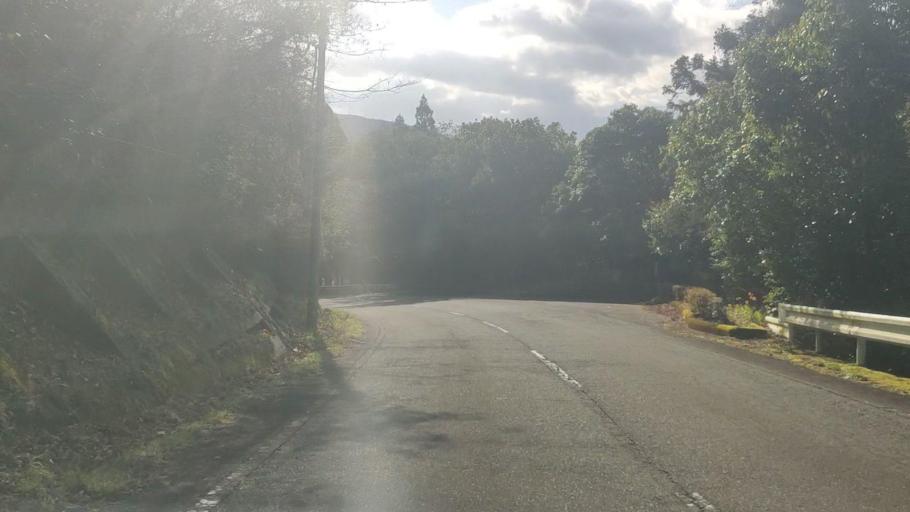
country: JP
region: Kumamoto
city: Hitoyoshi
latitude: 32.3172
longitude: 130.8438
